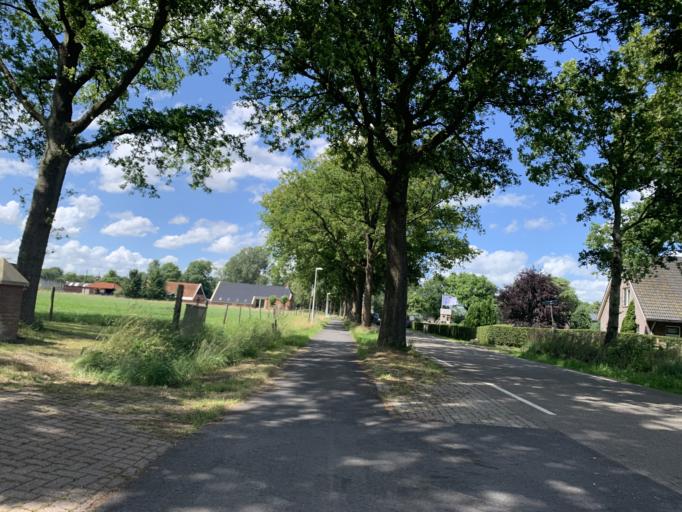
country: NL
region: Groningen
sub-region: Gemeente Haren
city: Haren
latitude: 53.1500
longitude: 6.6467
